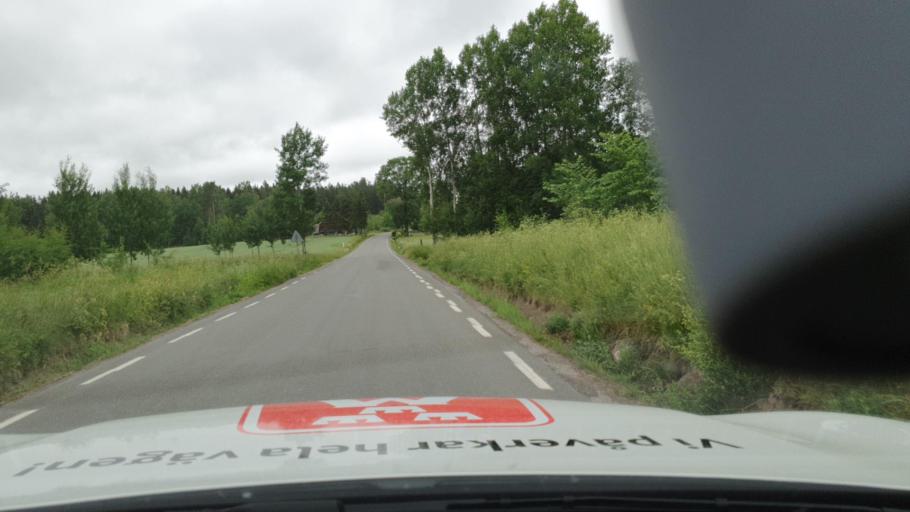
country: SE
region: Vaestra Goetaland
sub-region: Tibro Kommun
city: Tibro
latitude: 58.4082
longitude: 14.0647
